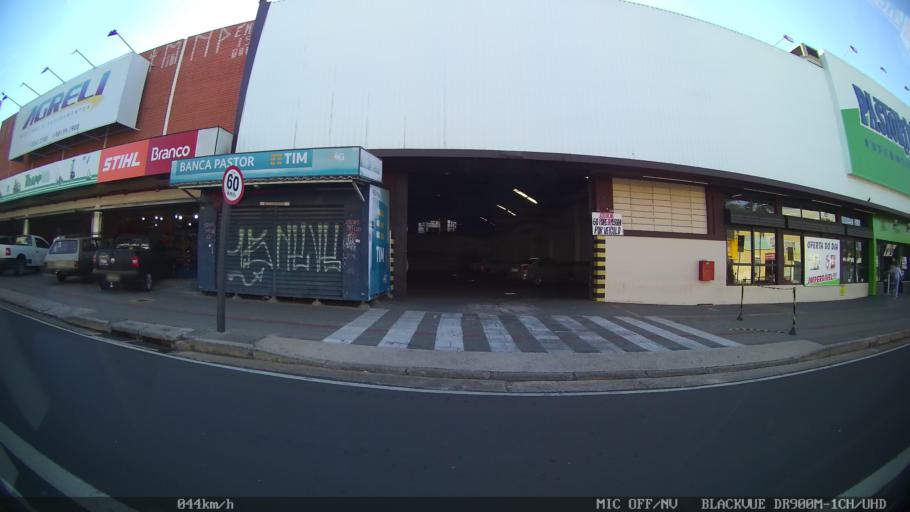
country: BR
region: Sao Paulo
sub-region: Sao Jose Do Rio Preto
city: Sao Jose do Rio Preto
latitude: -20.8074
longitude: -49.3800
